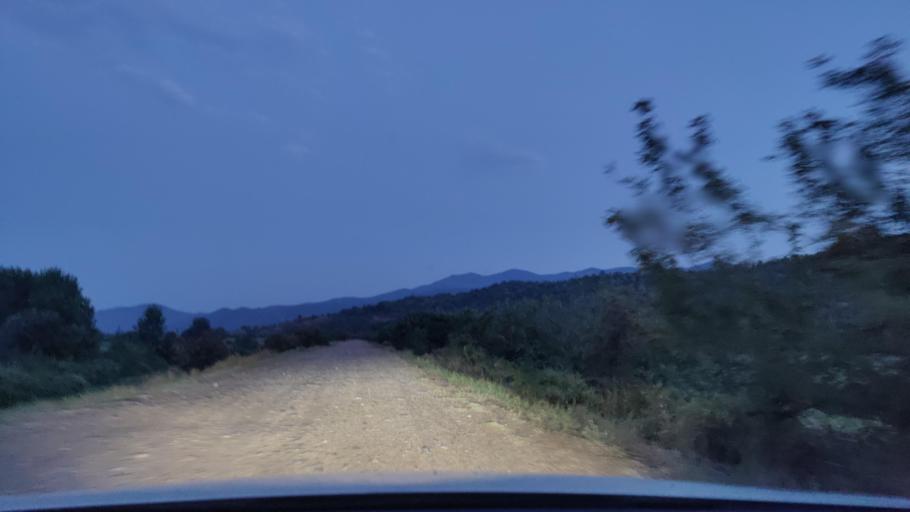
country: GR
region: Central Macedonia
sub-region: Nomos Serron
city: Chrysochorafa
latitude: 41.2039
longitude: 23.0786
